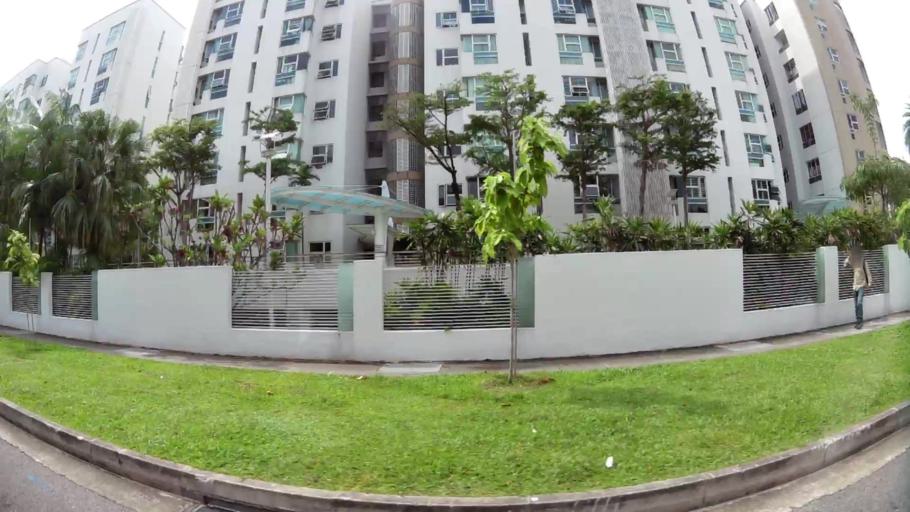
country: SG
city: Singapore
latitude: 1.3597
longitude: 103.9656
